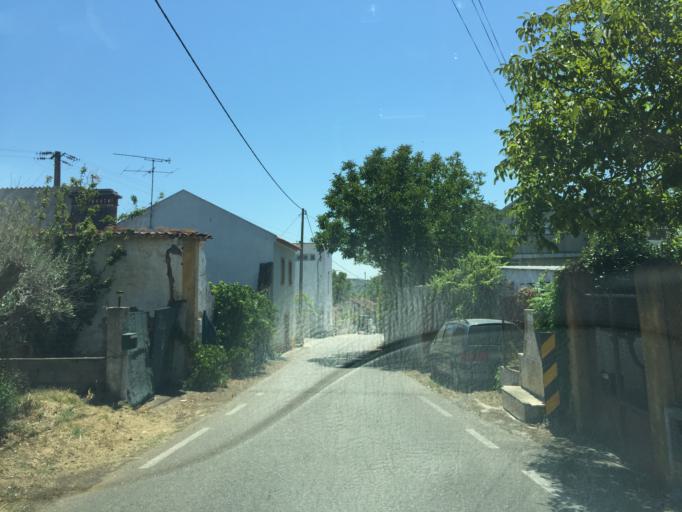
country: PT
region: Santarem
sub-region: Constancia
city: Constancia
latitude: 39.5738
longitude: -8.2946
